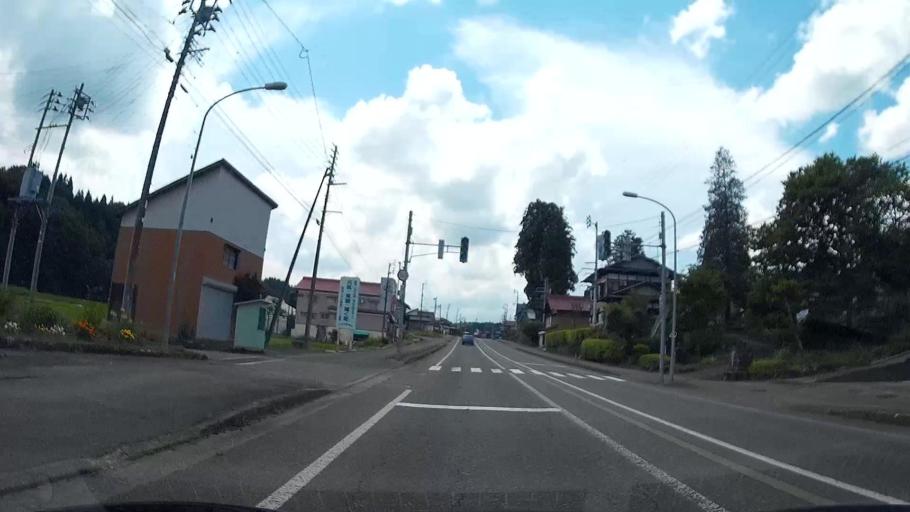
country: JP
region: Niigata
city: Tokamachi
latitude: 37.0413
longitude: 138.6793
